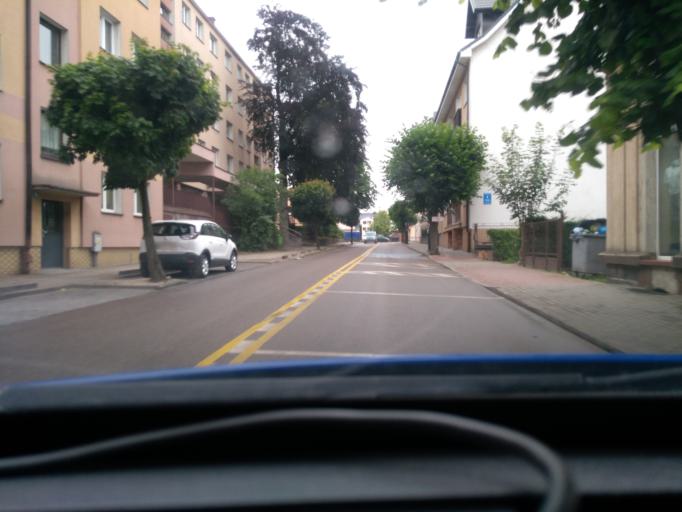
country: PL
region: Pomeranian Voivodeship
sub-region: Powiat kartuski
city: Kartuzy
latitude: 54.3344
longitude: 18.2031
